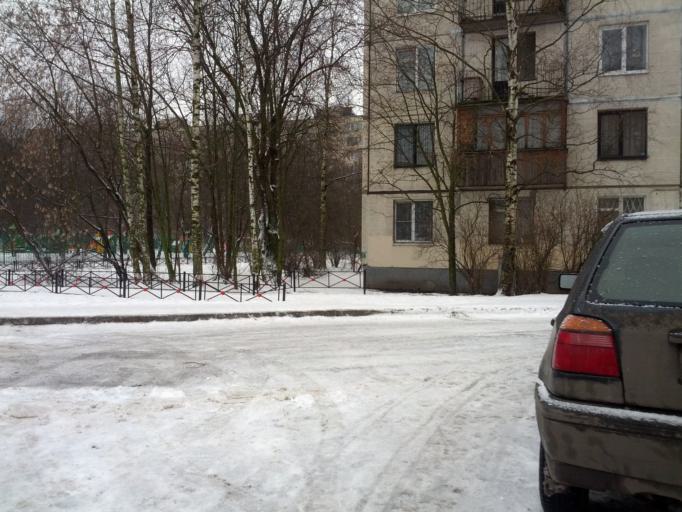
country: RU
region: St.-Petersburg
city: Krasnogvargeisky
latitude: 59.9072
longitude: 30.4777
